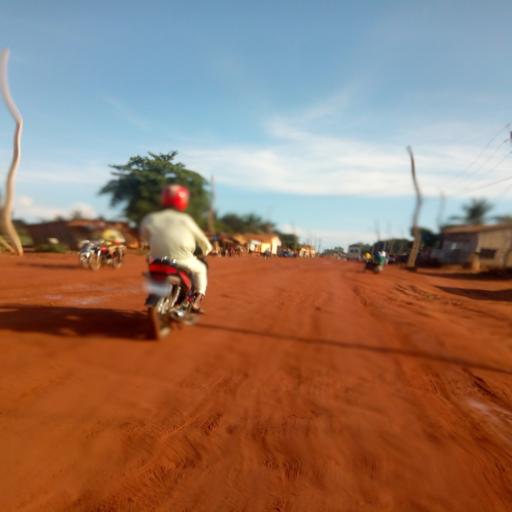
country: BJ
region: Atlantique
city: Hevie
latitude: 6.4170
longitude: 2.2629
